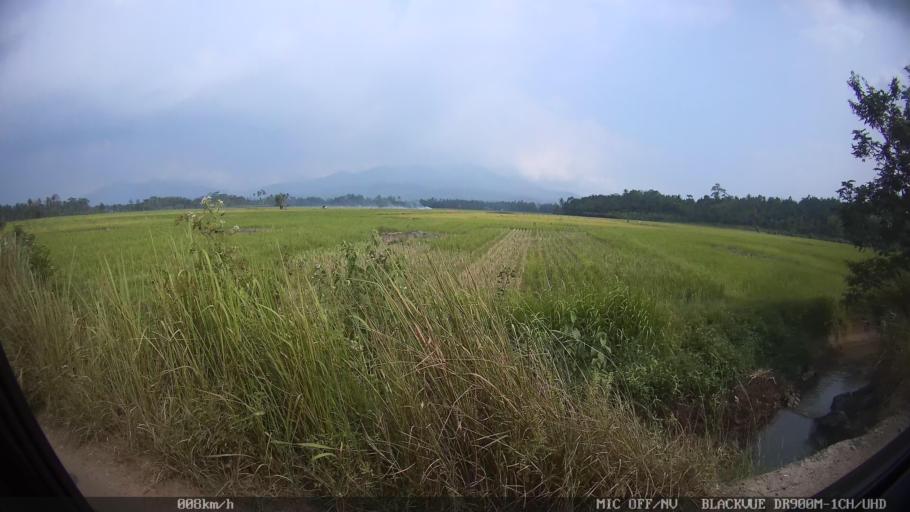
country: ID
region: Lampung
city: Gadingrejo
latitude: -5.4081
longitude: 105.0178
